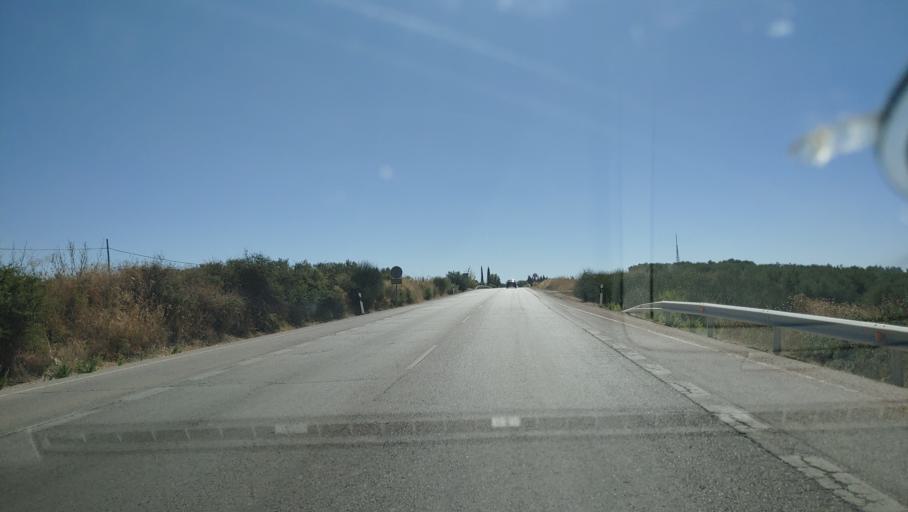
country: ES
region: Andalusia
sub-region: Provincia de Jaen
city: Villacarrillo
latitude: 38.1278
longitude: -3.0601
